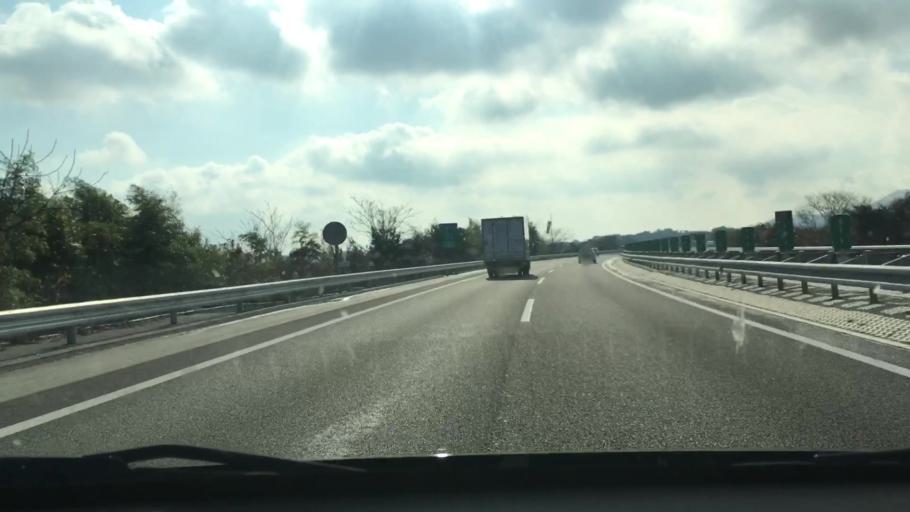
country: JP
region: Kumamoto
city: Uto
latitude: 32.7169
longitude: 130.7684
